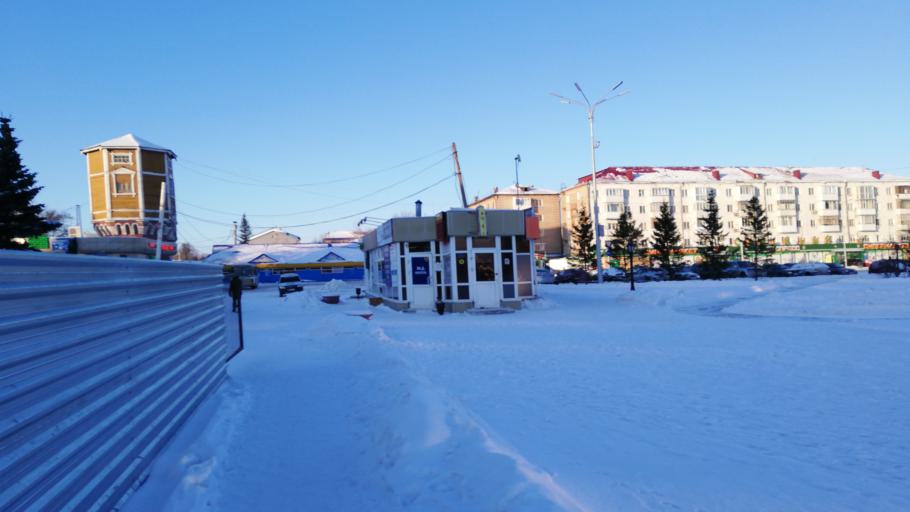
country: KZ
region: Soltustik Qazaqstan
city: Petropavlovsk
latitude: 54.8568
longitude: 69.1699
